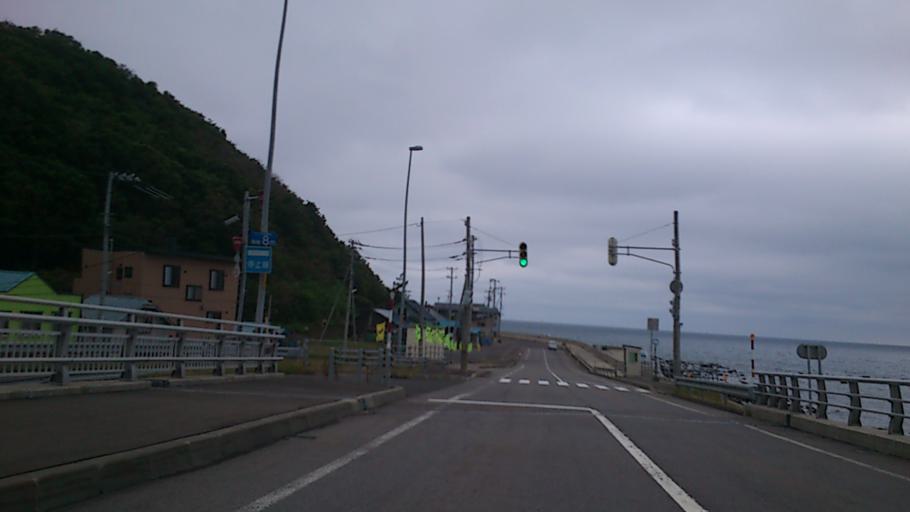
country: JP
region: Hokkaido
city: Iwanai
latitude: 42.7459
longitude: 140.1296
